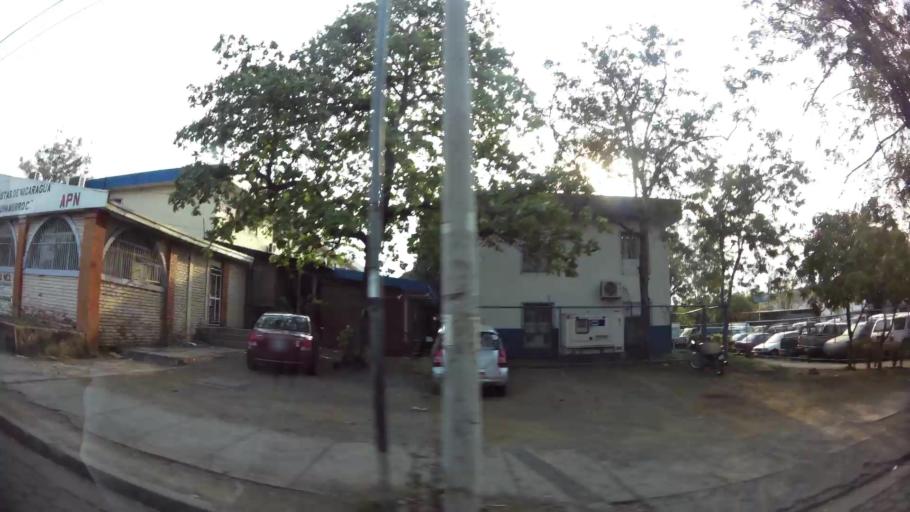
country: NI
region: Managua
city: Managua
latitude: 12.1262
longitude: -86.2973
